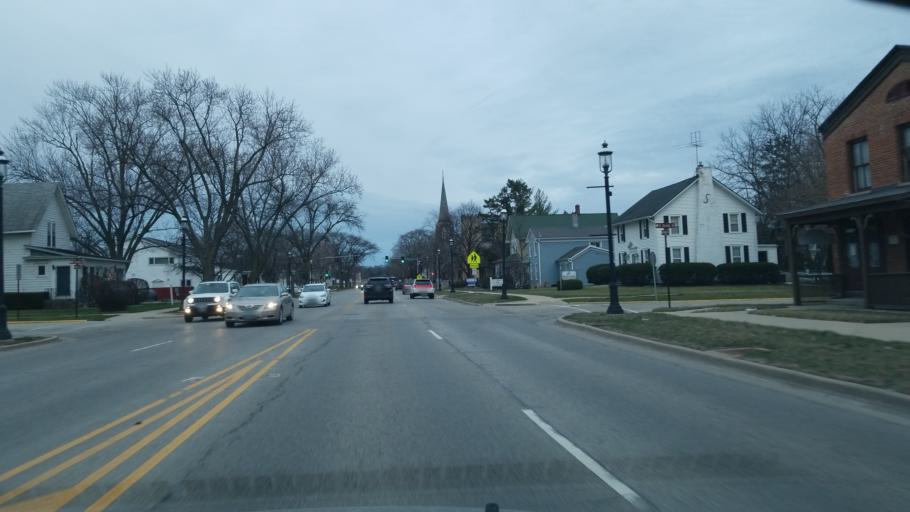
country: US
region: Illinois
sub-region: Kane County
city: West Dundee
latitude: 42.0981
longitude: -88.2843
